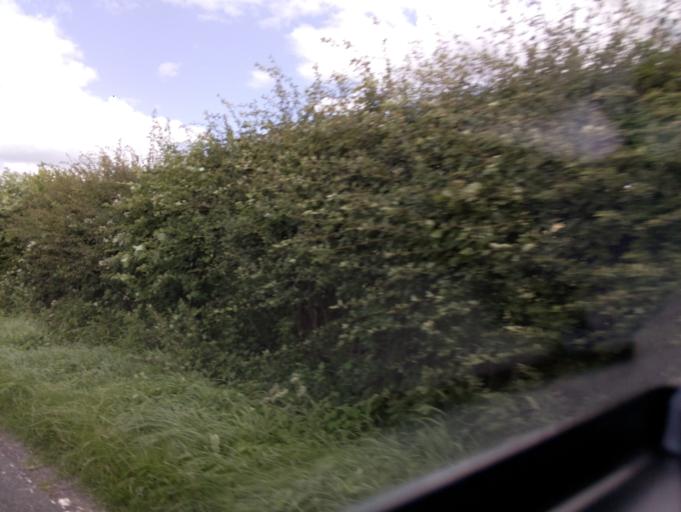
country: GB
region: England
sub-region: Nottinghamshire
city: Ruddington
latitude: 52.8757
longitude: -1.1256
